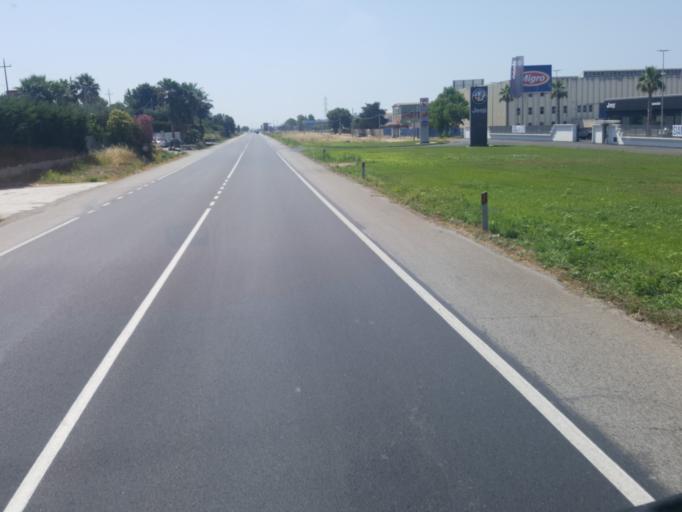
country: IT
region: Apulia
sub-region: Provincia di Taranto
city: Massafra
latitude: 40.5688
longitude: 17.1254
